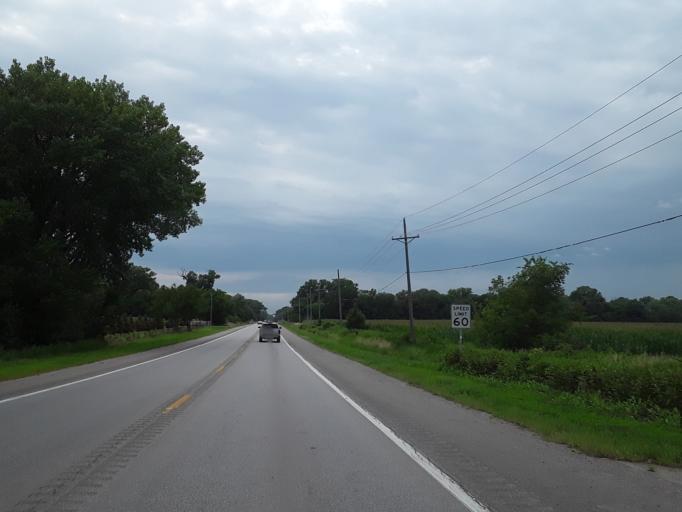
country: US
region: Nebraska
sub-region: Saunders County
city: Yutan
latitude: 41.2338
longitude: -96.3322
